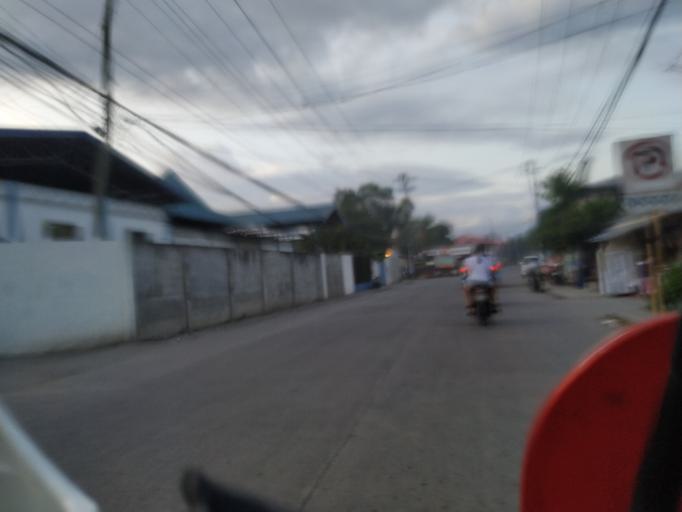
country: PH
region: Central Visayas
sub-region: Province of Negros Oriental
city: Dumaguete
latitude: 9.3008
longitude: 123.2933
